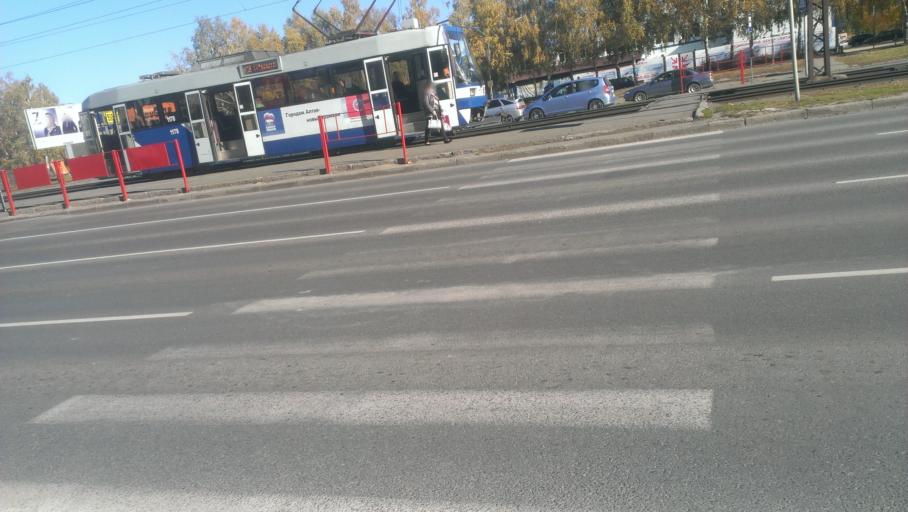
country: RU
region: Altai Krai
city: Novosilikatnyy
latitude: 53.3308
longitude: 83.6925
